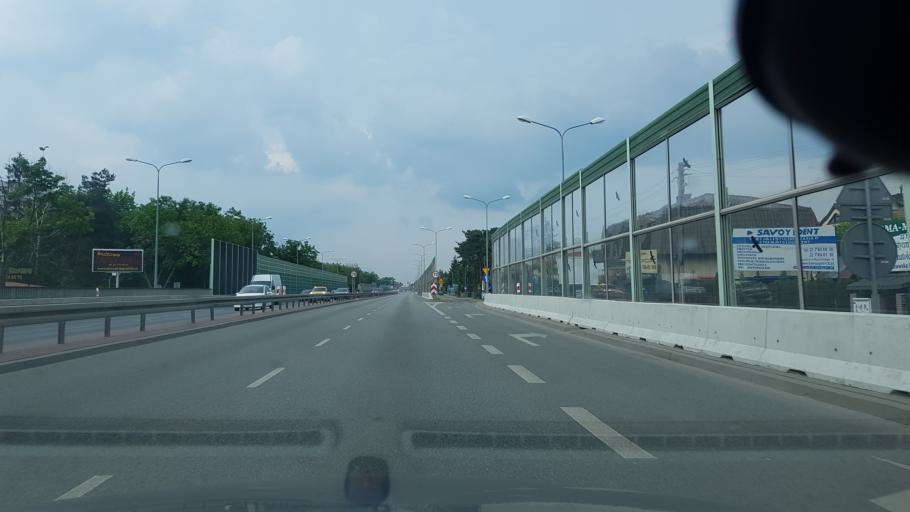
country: PL
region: Masovian Voivodeship
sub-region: Powiat legionowski
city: Legionowo
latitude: 52.3892
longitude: 20.9307
